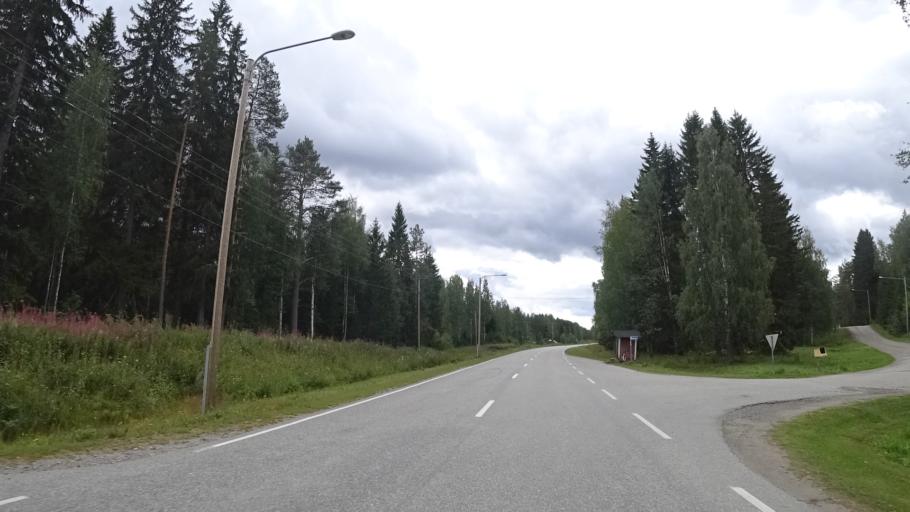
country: FI
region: North Karelia
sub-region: Joensuu
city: Ilomantsi
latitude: 62.6396
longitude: 31.2860
